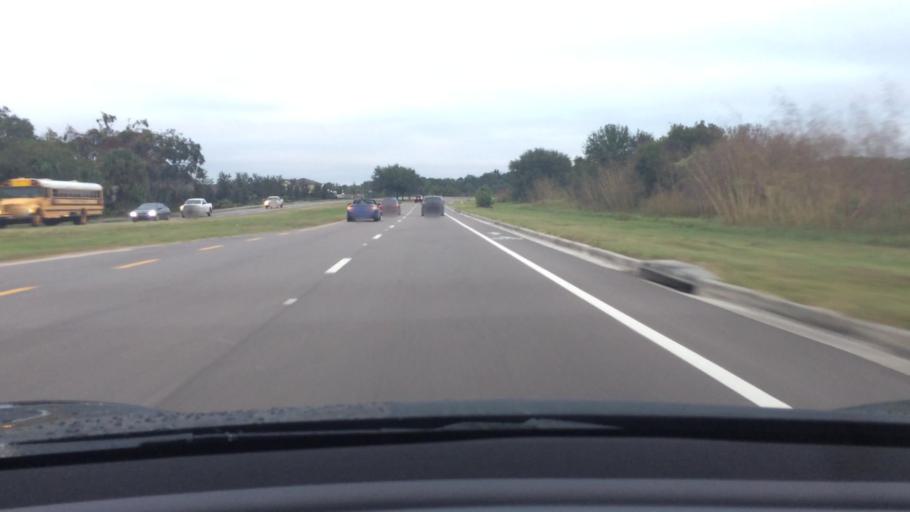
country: US
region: Florida
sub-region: Hillsborough County
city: Progress Village
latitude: 27.8888
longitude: -82.3588
